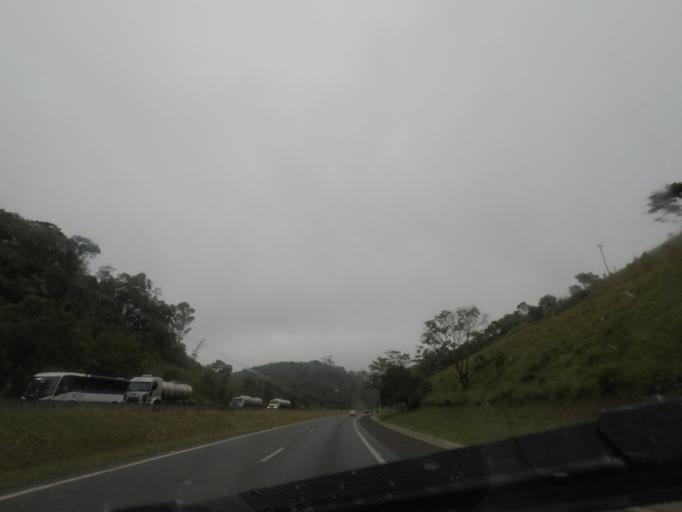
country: BR
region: Sao Paulo
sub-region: Piracaia
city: Piracaia
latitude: -23.1738
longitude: -46.2796
